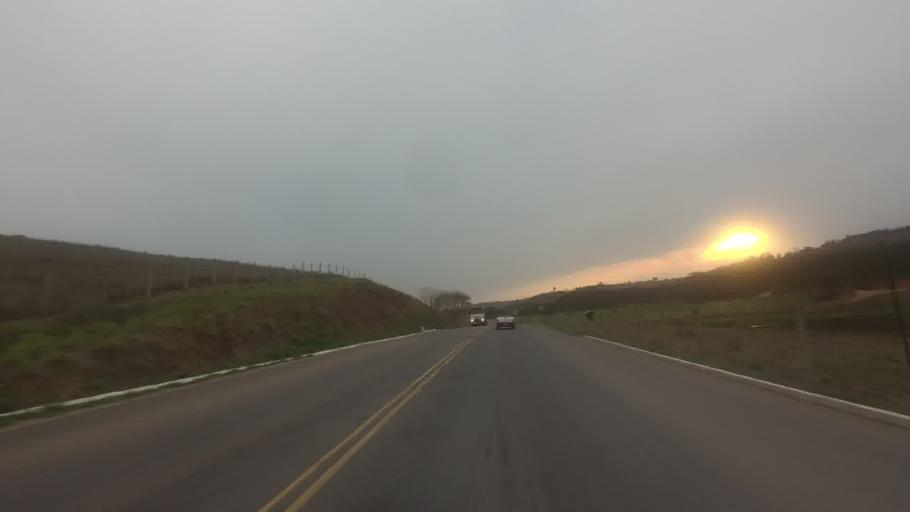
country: BR
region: Minas Gerais
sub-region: Recreio
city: Recreio
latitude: -21.6588
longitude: -42.3724
